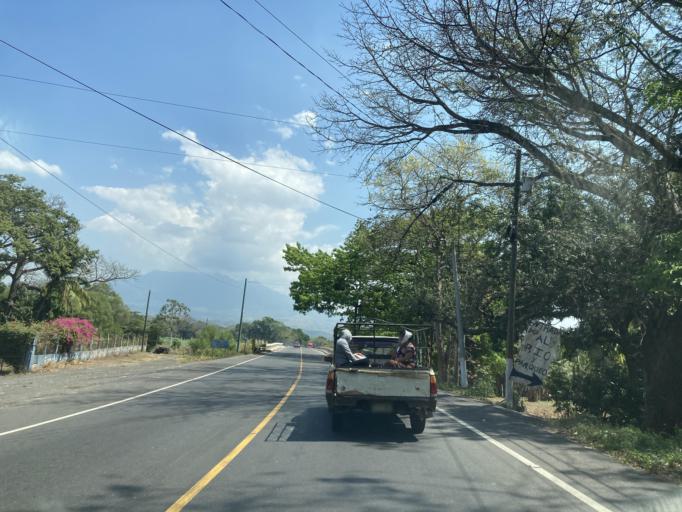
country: GT
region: Escuintla
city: Guanagazapa
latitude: 14.1143
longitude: -90.6410
